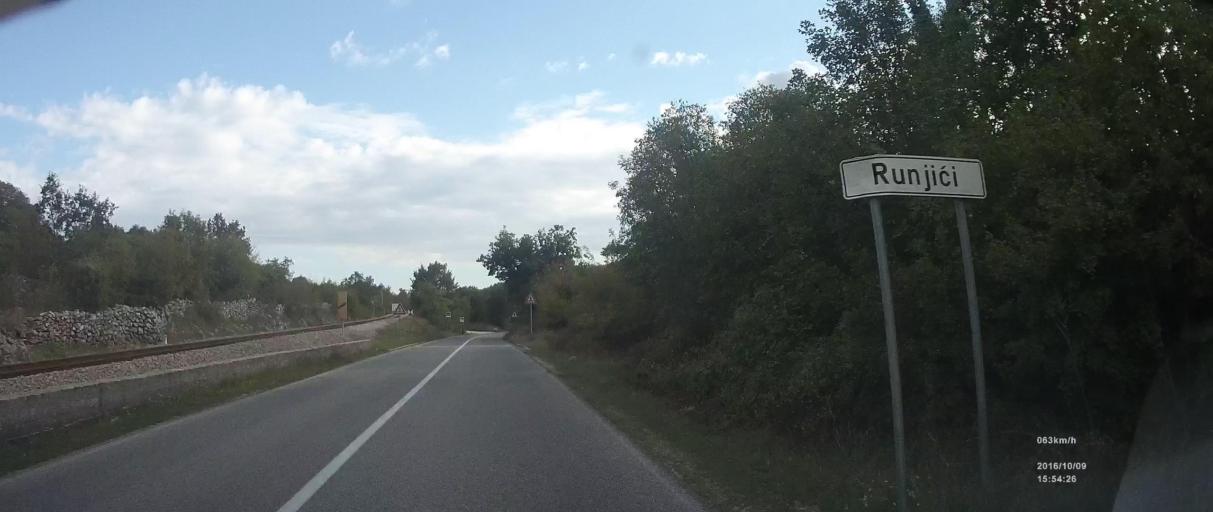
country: HR
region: Splitsko-Dalmatinska
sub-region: Grad Trogir
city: Trogir
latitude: 43.5948
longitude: 16.2254
